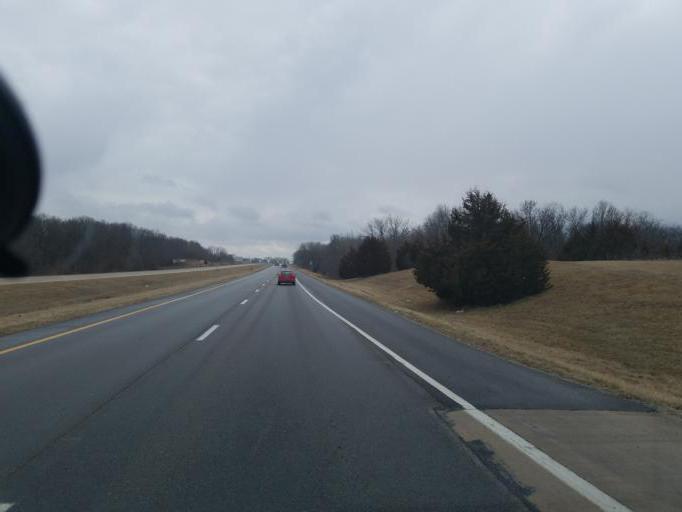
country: US
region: Missouri
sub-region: Randolph County
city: Moberly
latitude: 39.3885
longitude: -92.4134
